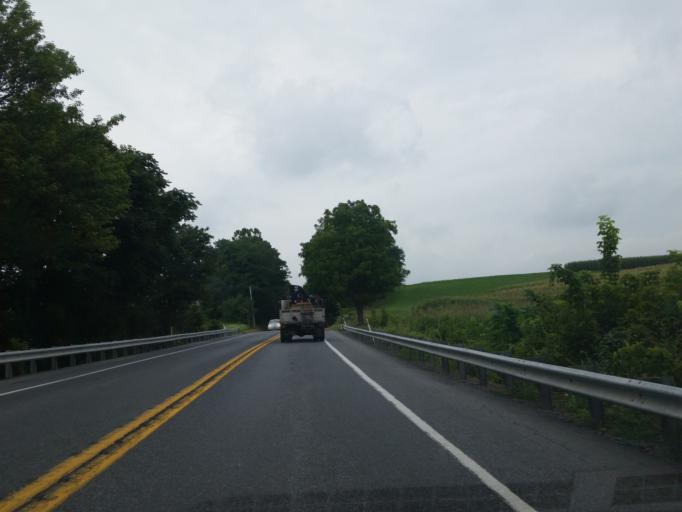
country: US
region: Pennsylvania
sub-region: Lancaster County
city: Brickerville
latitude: 40.2037
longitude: -76.2991
